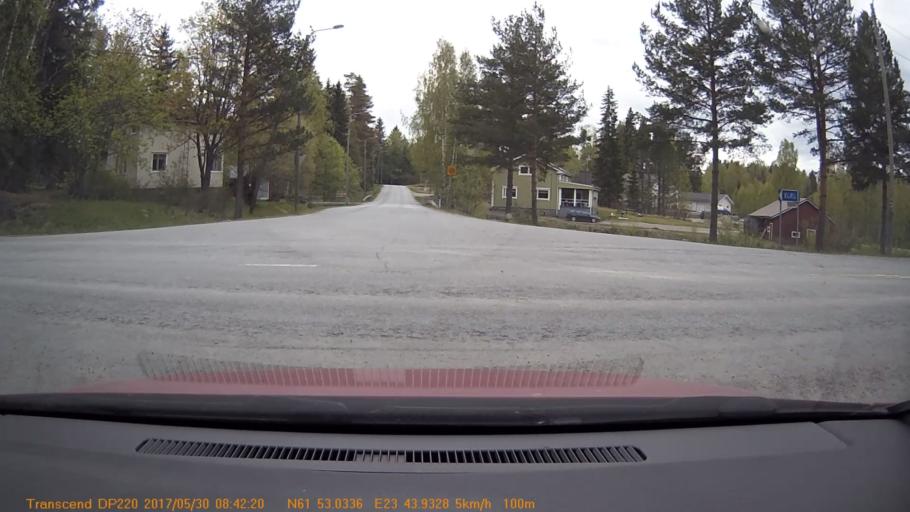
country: FI
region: Pirkanmaa
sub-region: Tampere
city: Kuru
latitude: 61.8839
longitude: 23.7322
